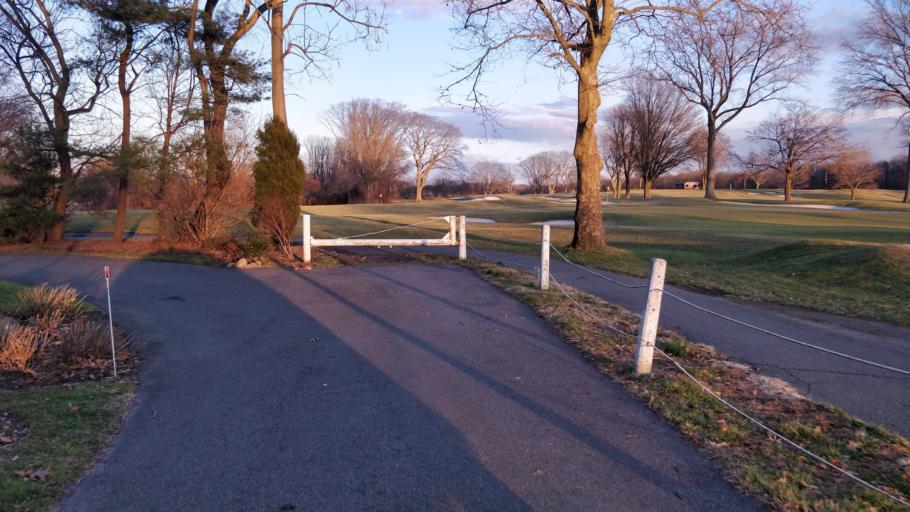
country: US
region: New York
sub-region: Nassau County
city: Locust Valley
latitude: 40.8708
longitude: -73.6121
